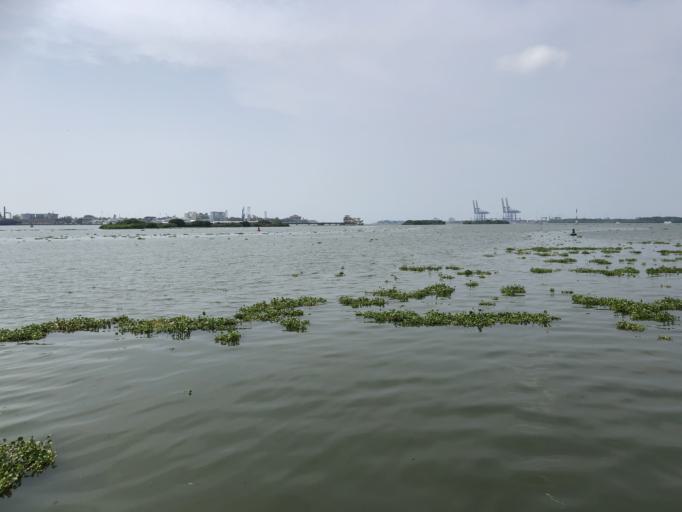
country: IN
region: Kerala
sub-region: Ernakulam
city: Cochin
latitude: 9.9737
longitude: 76.2771
